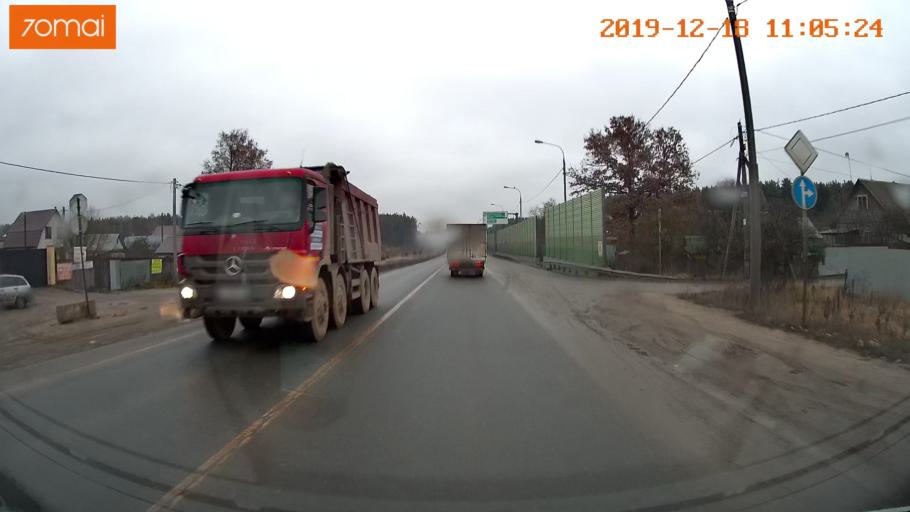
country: RU
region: Moskovskaya
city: Golitsyno
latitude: 55.5976
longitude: 37.0080
